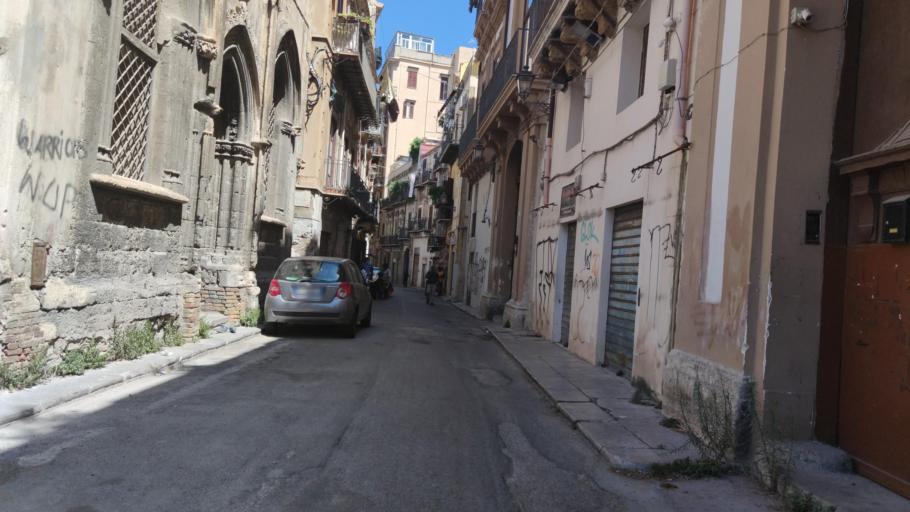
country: IT
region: Sicily
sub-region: Palermo
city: Palermo
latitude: 38.1128
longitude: 13.3643
